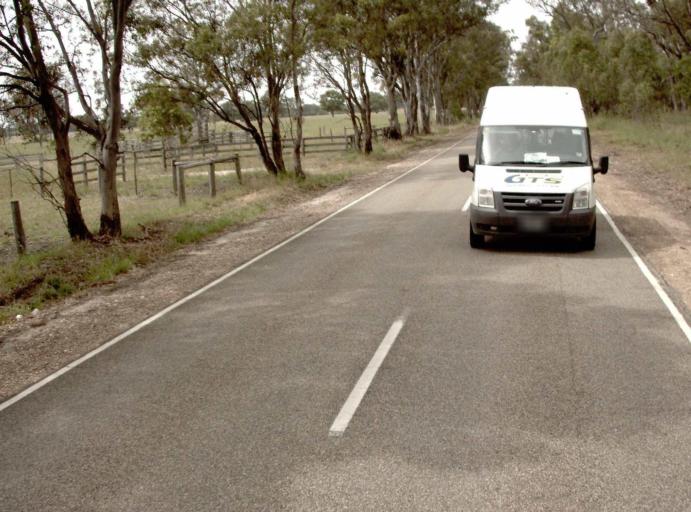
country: AU
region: Victoria
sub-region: Wellington
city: Sale
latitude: -37.9081
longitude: 147.0788
